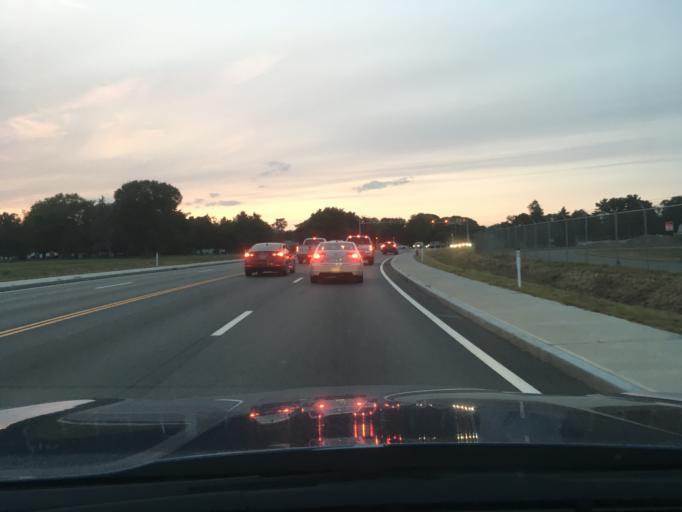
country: US
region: Rhode Island
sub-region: Kent County
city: Warwick
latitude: 41.7084
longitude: -71.4402
